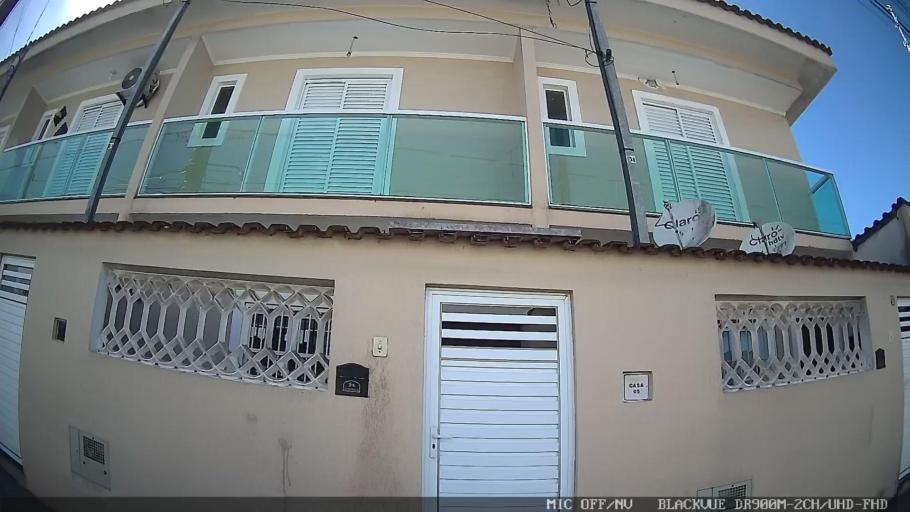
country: BR
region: Sao Paulo
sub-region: Santos
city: Santos
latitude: -23.9395
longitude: -46.2955
